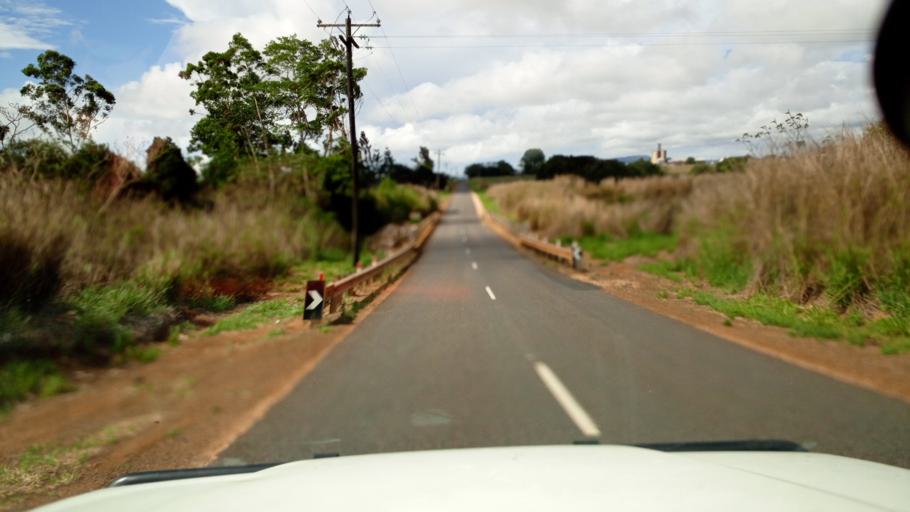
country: AU
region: Queensland
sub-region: Tablelands
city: Tolga
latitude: -17.2241
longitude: 145.5375
